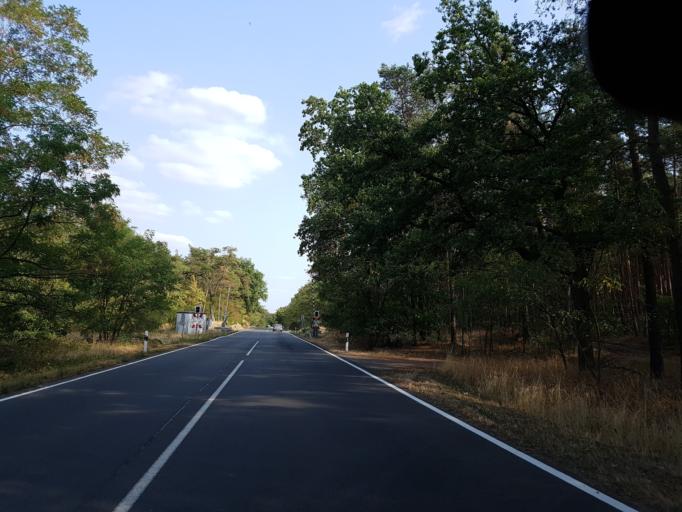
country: DE
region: Saxony-Anhalt
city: Pretzsch
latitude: 51.7320
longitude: 12.7722
